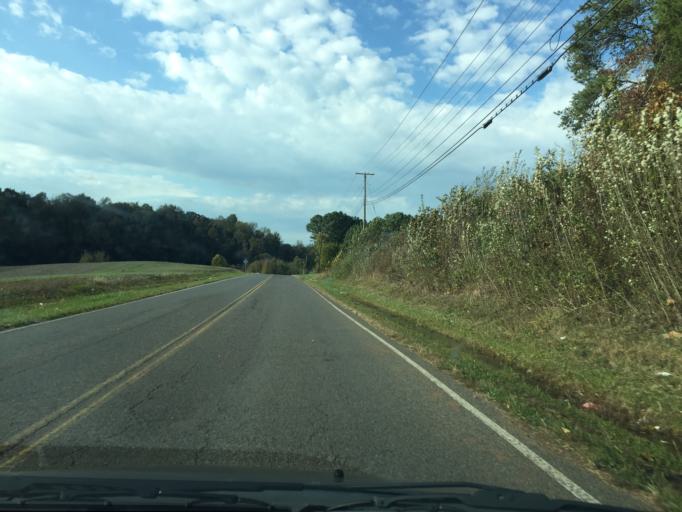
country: US
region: Tennessee
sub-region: Loudon County
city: Loudon
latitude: 35.7139
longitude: -84.3450
